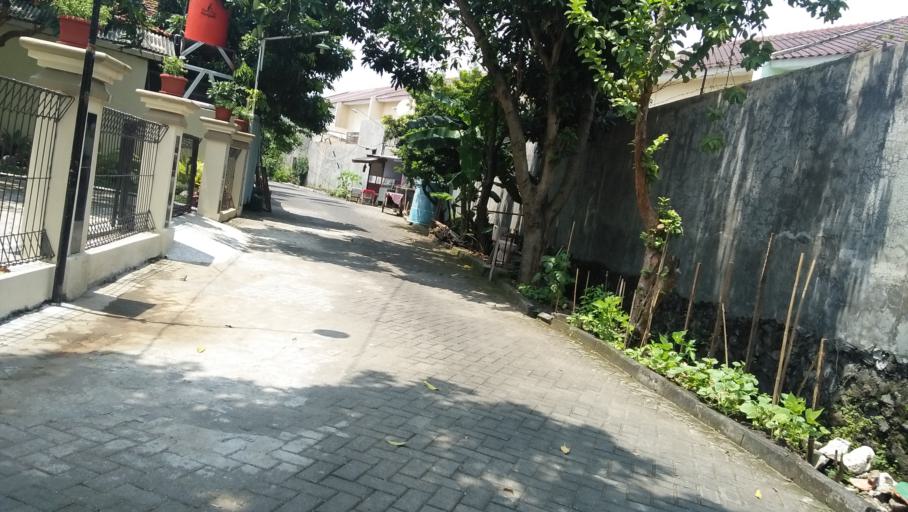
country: ID
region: Central Java
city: Mranggen
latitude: -7.0280
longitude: 110.4634
